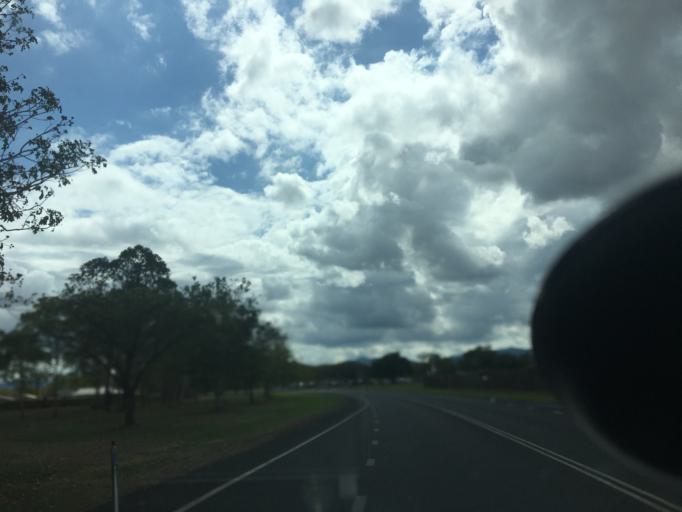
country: AU
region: Queensland
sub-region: Tablelands
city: Mareeba
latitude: -17.0107
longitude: 145.4284
